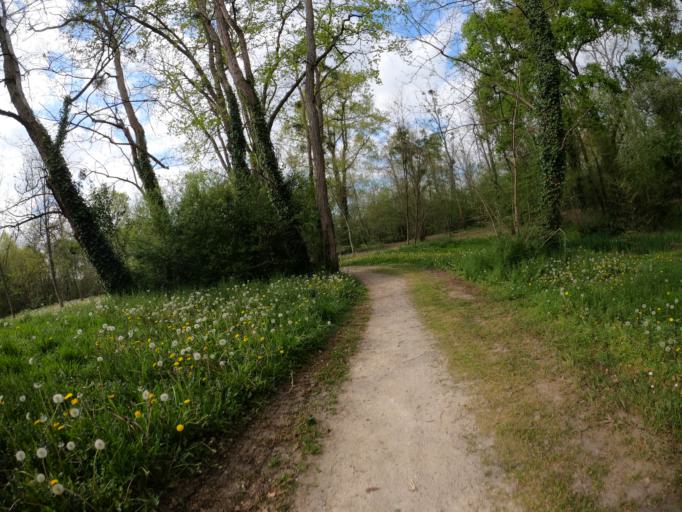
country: FR
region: Aquitaine
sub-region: Departement des Pyrenees-Atlantiques
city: Lons
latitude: 43.3286
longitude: -0.3868
